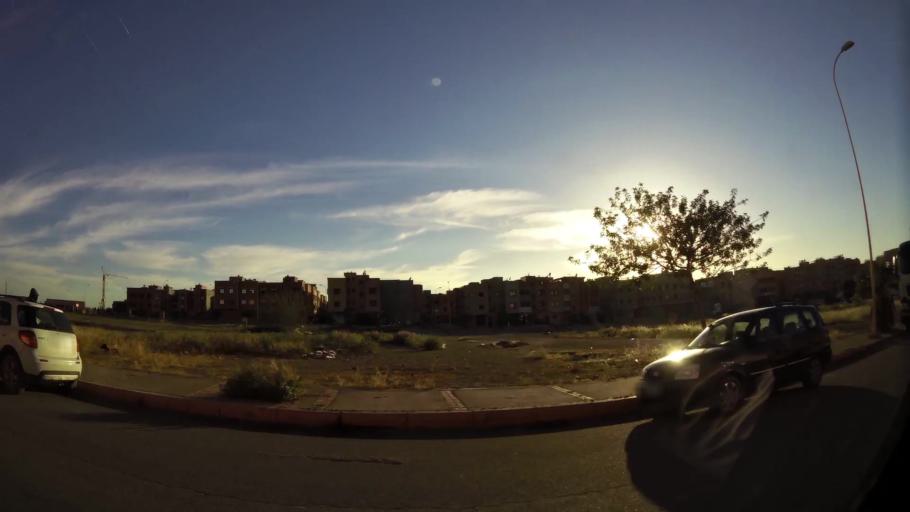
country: MA
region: Marrakech-Tensift-Al Haouz
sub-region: Marrakech
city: Marrakesh
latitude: 31.7487
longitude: -8.1134
